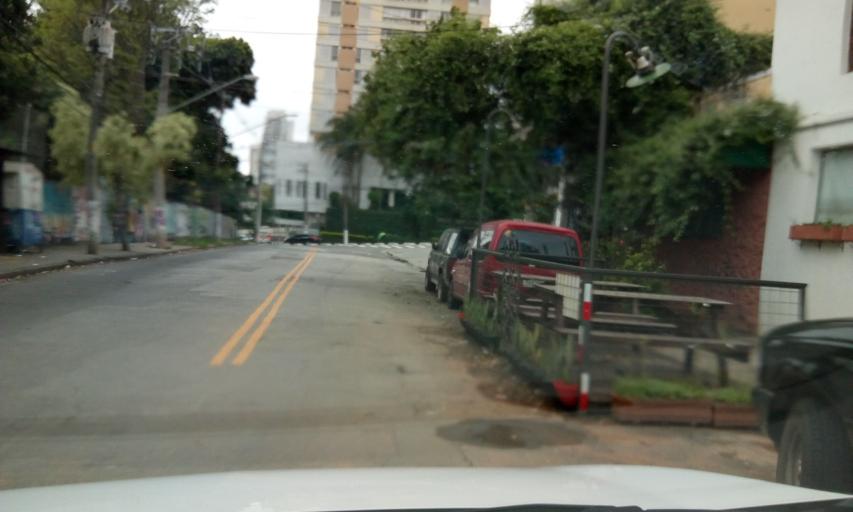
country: BR
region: Sao Paulo
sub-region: Sao Paulo
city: Sao Paulo
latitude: -23.5503
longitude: -46.6821
